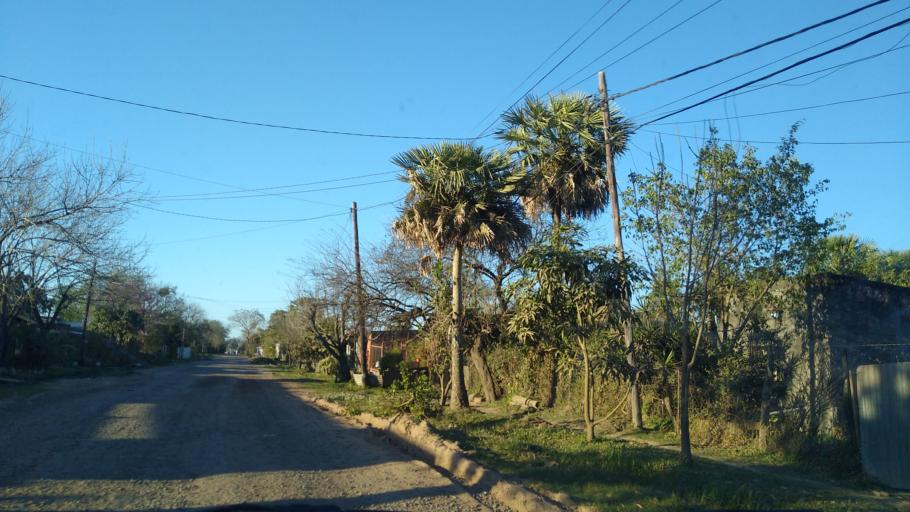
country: AR
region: Chaco
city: Barranqueras
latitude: -27.4711
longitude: -58.9483
